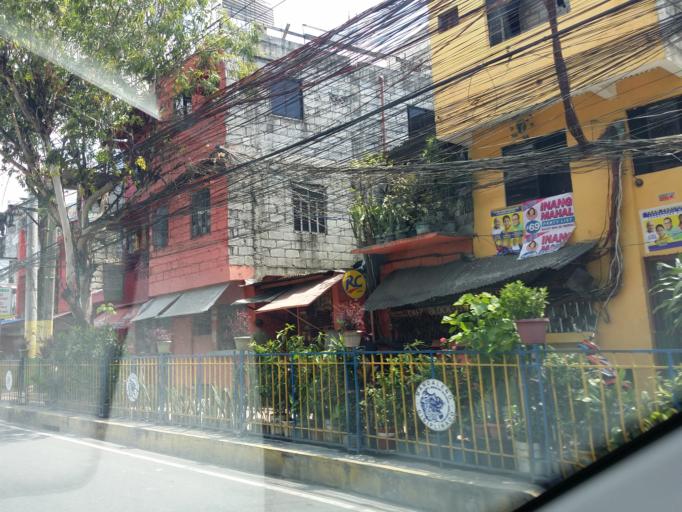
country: PH
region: Metro Manila
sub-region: Mandaluyong
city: Mandaluyong City
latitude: 14.5836
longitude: 121.0370
